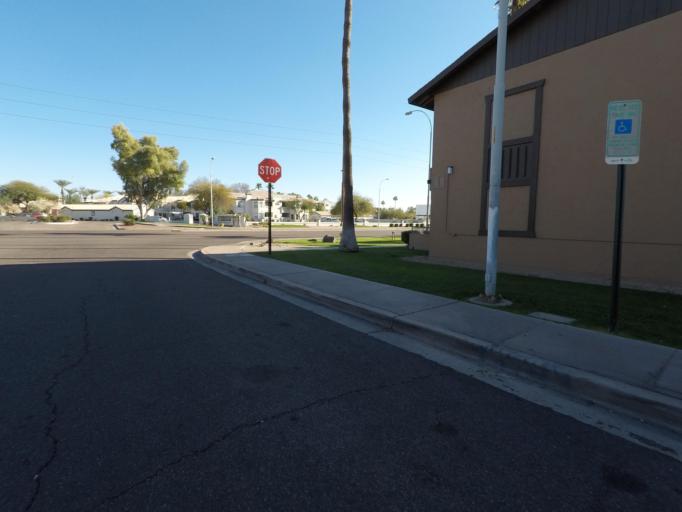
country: US
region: Arizona
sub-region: Maricopa County
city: Tempe Junction
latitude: 33.3813
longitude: -111.9279
